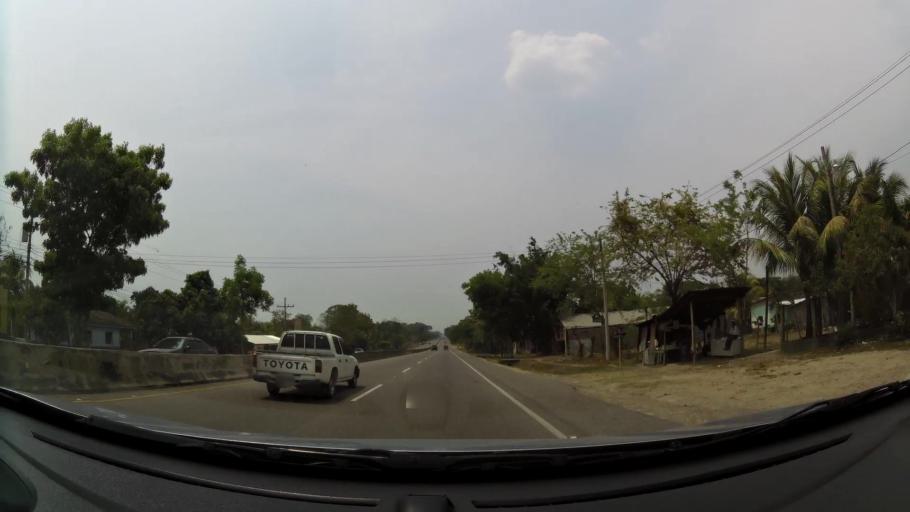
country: HN
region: Cortes
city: Oropendolas
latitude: 15.0629
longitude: -87.9289
